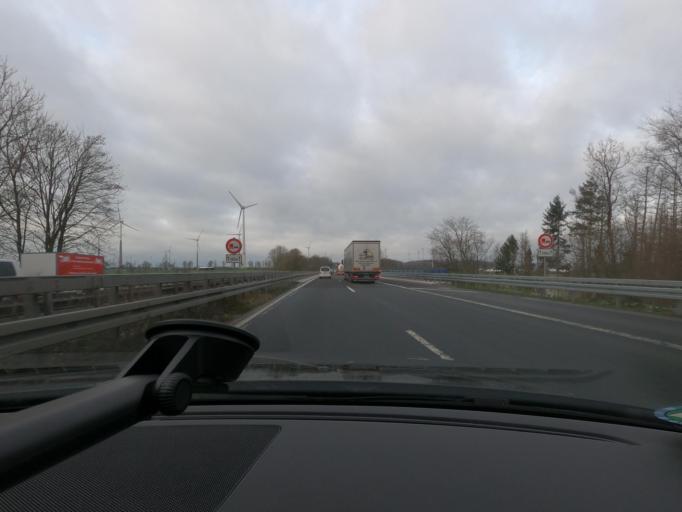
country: DE
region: North Rhine-Westphalia
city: Marsberg
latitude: 51.5386
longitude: 8.8478
